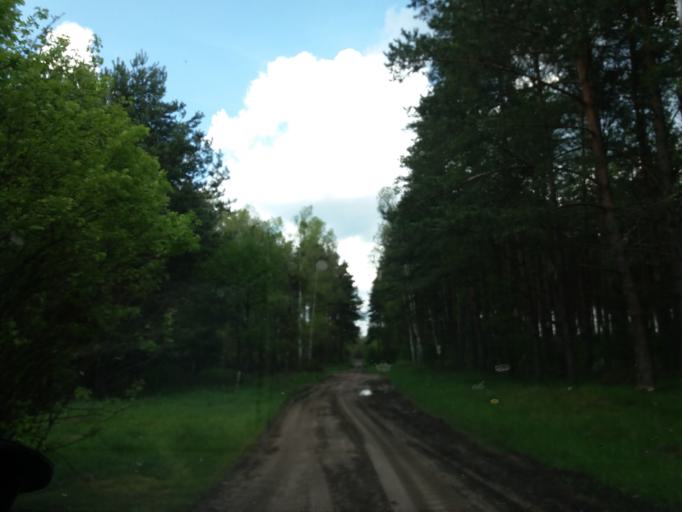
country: PL
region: West Pomeranian Voivodeship
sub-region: Powiat walecki
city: Czlopa
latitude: 53.1218
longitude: 15.9598
